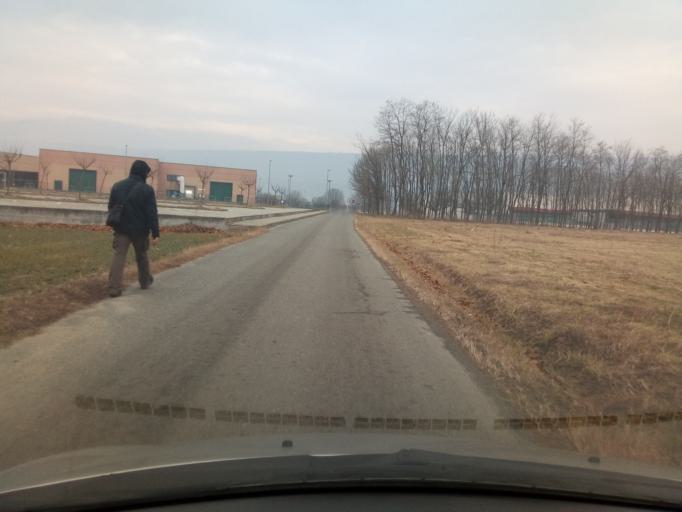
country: IT
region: Piedmont
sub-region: Provincia di Torino
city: Burolo
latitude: 45.4667
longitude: 7.9223
